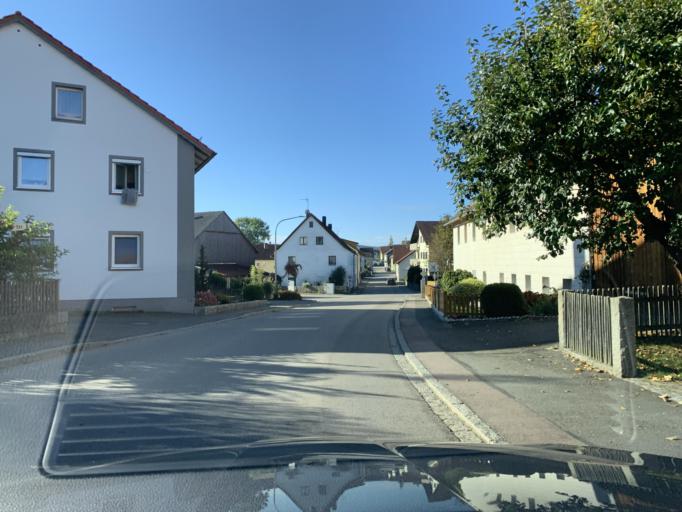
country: DE
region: Bavaria
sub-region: Upper Palatinate
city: Winklarn
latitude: 49.4079
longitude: 12.4645
